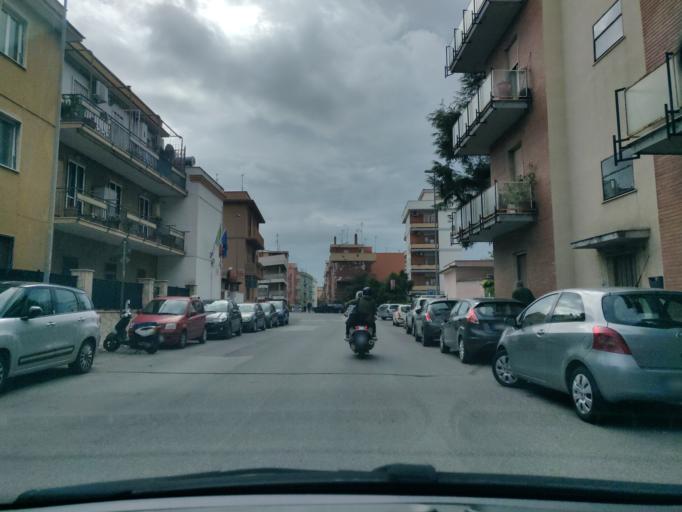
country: IT
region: Latium
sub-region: Citta metropolitana di Roma Capitale
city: Civitavecchia
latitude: 42.0953
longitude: 11.8035
